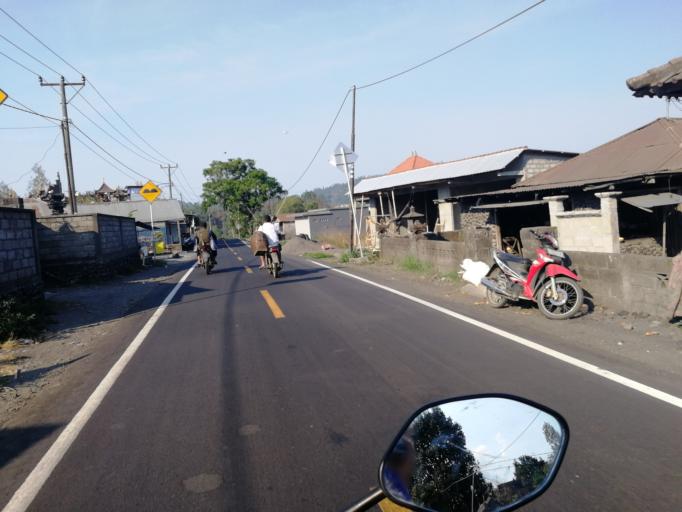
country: ID
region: Bali
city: Banjar Trunyan
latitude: -8.2443
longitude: 115.4009
